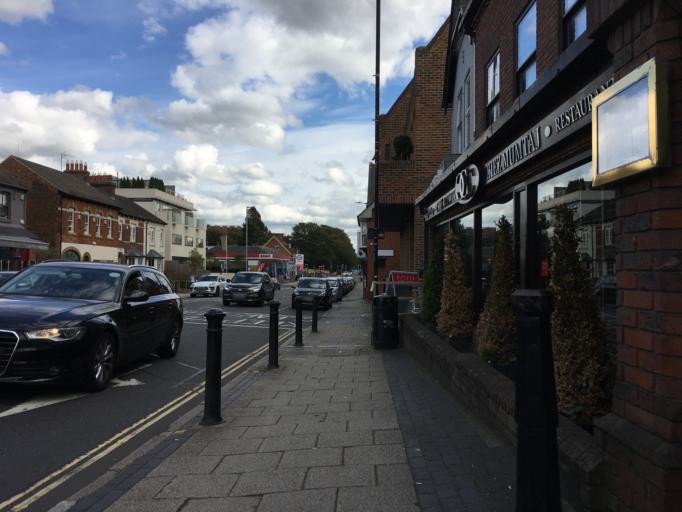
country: GB
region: England
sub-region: Hertfordshire
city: St Albans
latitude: 51.7487
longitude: -0.3336
